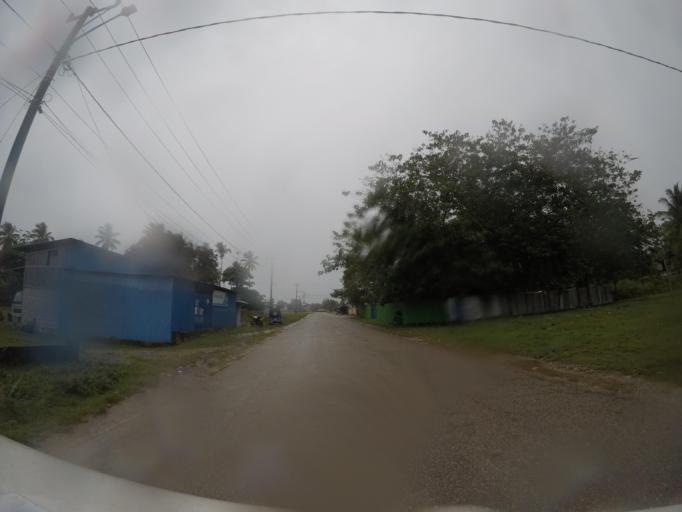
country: TL
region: Lautem
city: Lospalos
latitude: -8.5209
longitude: 127.0007
